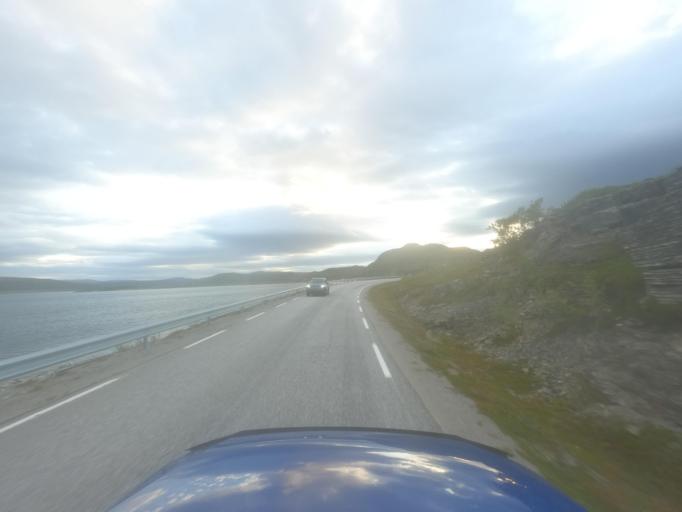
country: NO
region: Finnmark Fylke
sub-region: Porsanger
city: Lakselv
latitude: 70.5352
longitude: 25.1250
